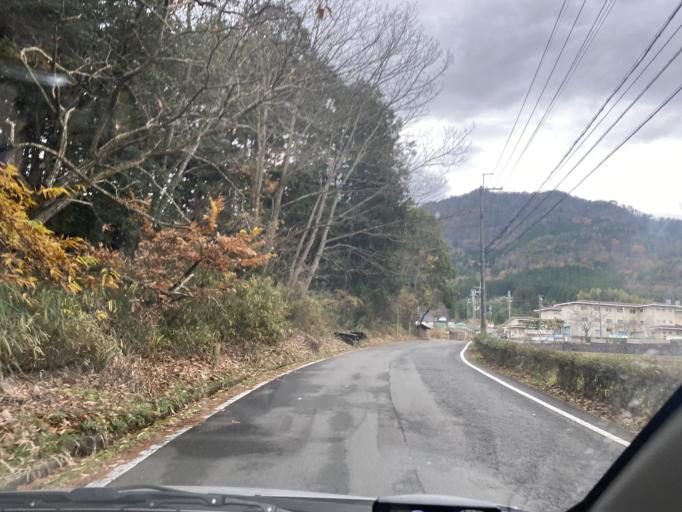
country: JP
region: Kyoto
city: Kameoka
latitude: 35.0564
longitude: 135.4573
